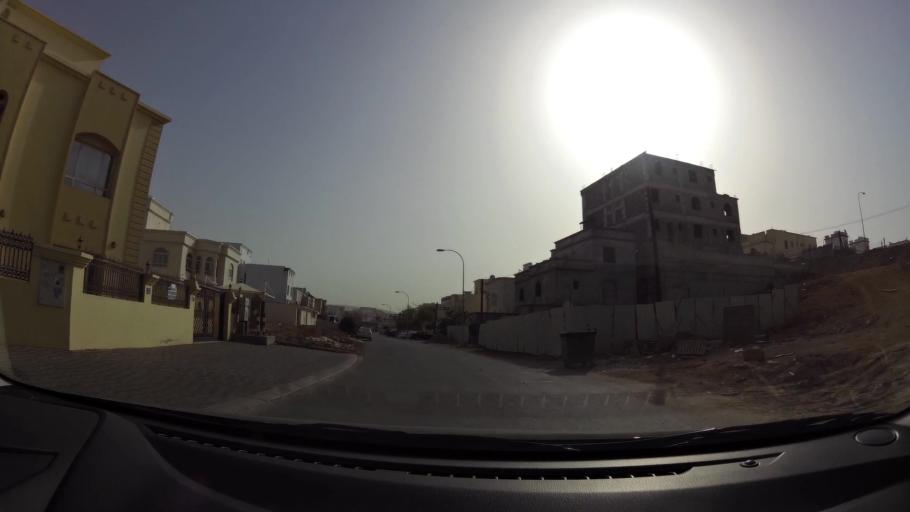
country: OM
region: Muhafazat Masqat
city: Bawshar
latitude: 23.5524
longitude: 58.3624
